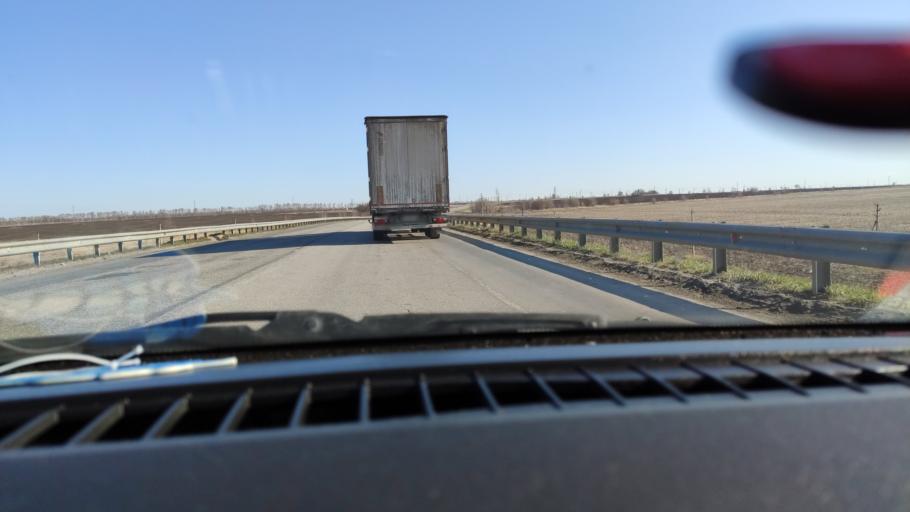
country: RU
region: Samara
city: Varlamovo
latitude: 53.1750
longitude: 48.2824
